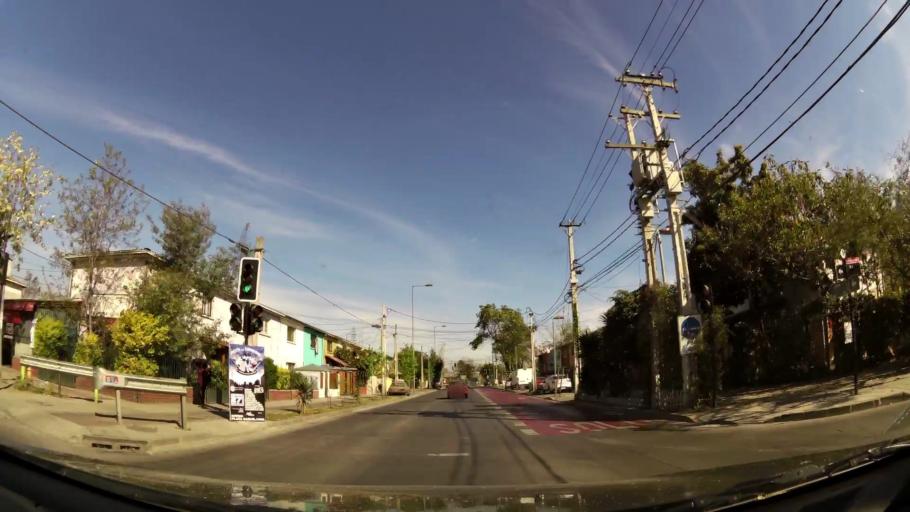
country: CL
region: Santiago Metropolitan
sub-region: Provincia de Santiago
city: Santiago
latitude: -33.4781
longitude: -70.6341
